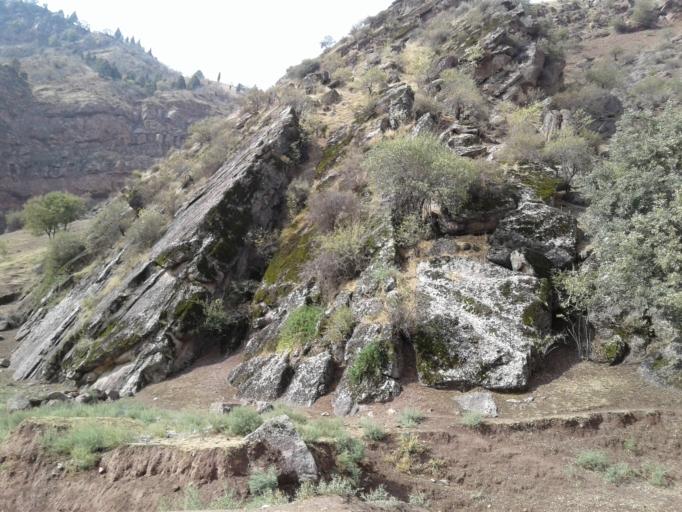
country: TJ
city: Shahrinav
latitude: 38.7035
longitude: 68.3678
